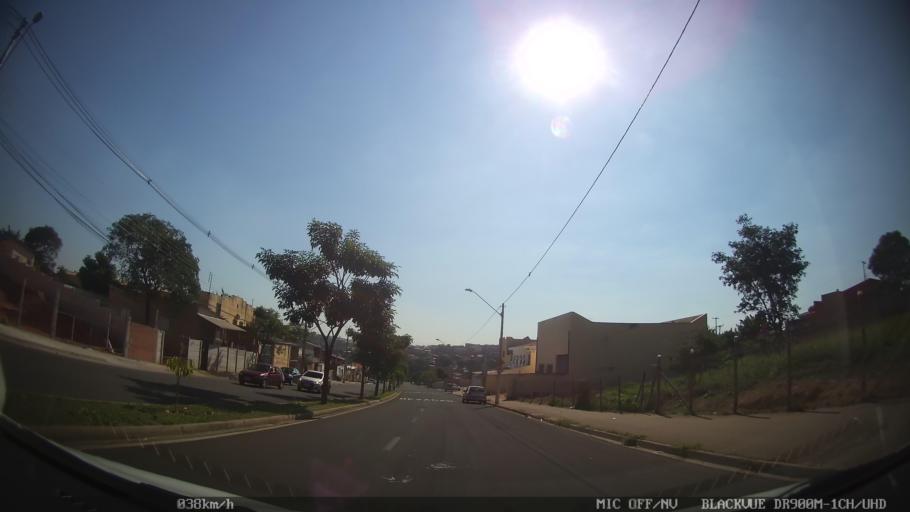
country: BR
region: Sao Paulo
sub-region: Campinas
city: Campinas
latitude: -22.9492
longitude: -47.0788
